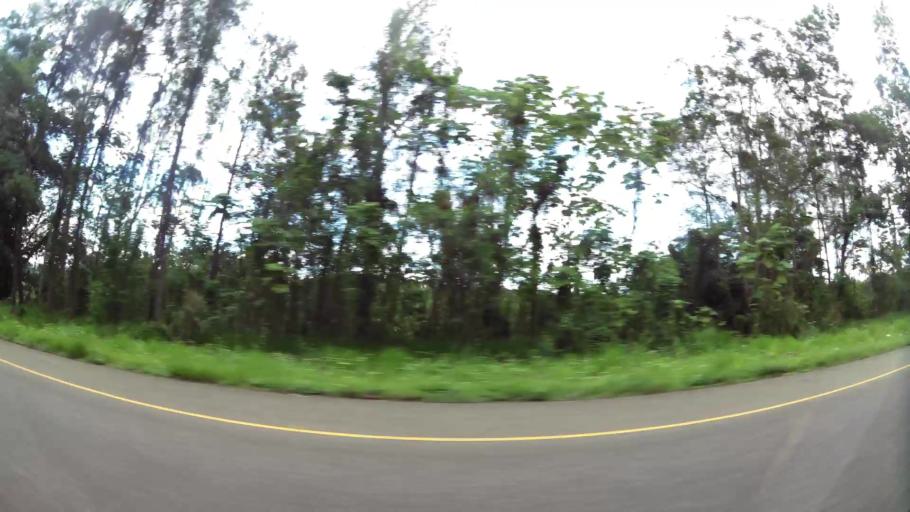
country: DO
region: La Vega
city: Rincon
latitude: 19.1041
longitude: -70.4430
